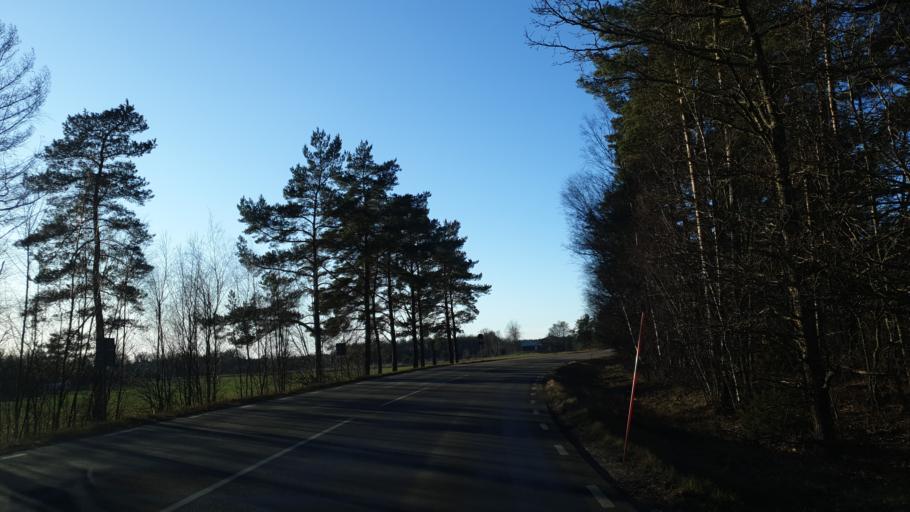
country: SE
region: Blekinge
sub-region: Ronneby Kommun
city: Ronneby
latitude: 56.1935
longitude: 15.3651
